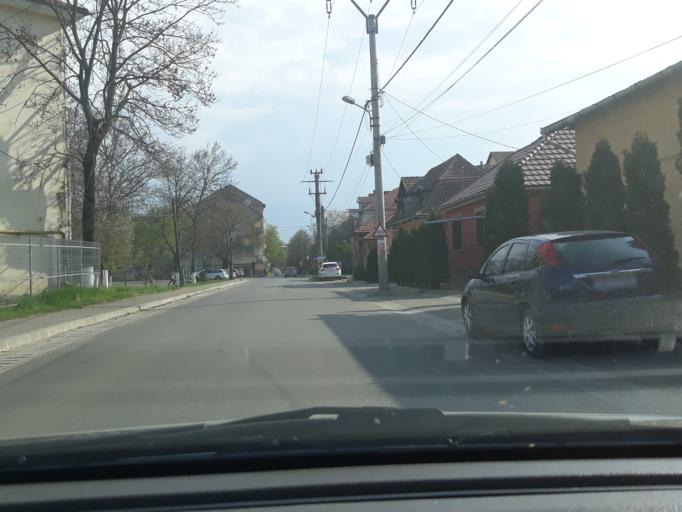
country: RO
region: Bihor
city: Margita
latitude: 47.3484
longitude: 22.3354
